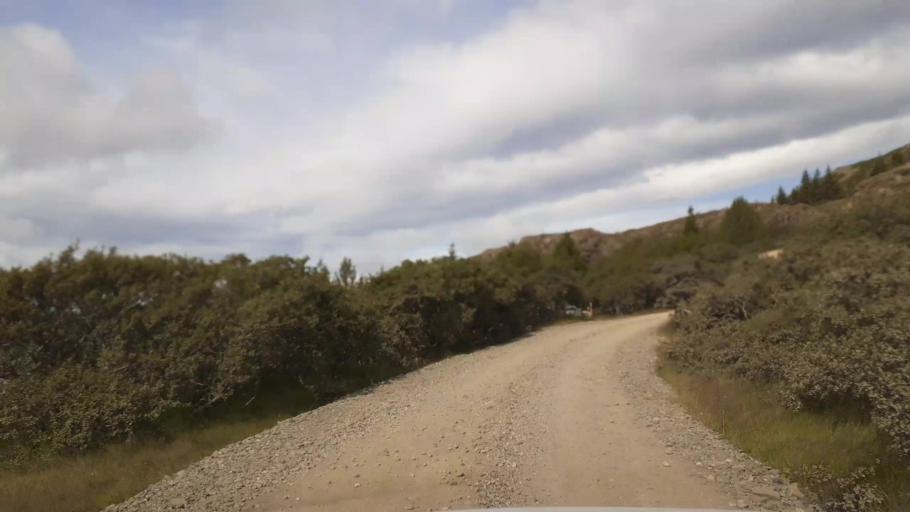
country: IS
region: East
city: Hoefn
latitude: 64.4375
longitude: -14.9110
